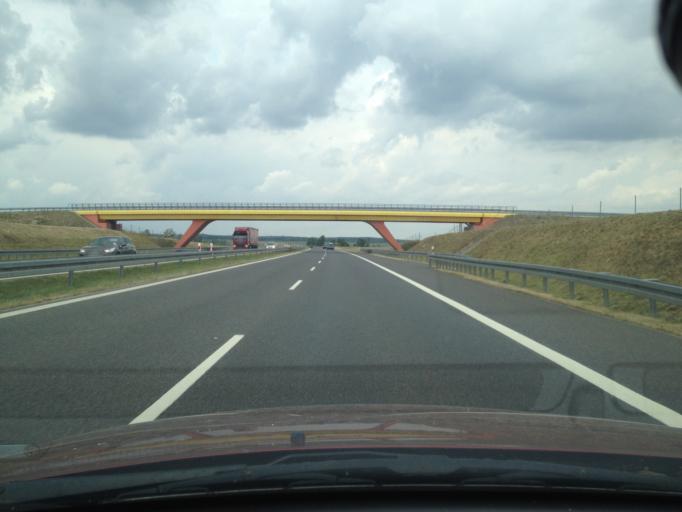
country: PL
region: West Pomeranian Voivodeship
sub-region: Powiat mysliborski
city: Mysliborz
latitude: 52.9778
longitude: 14.9006
